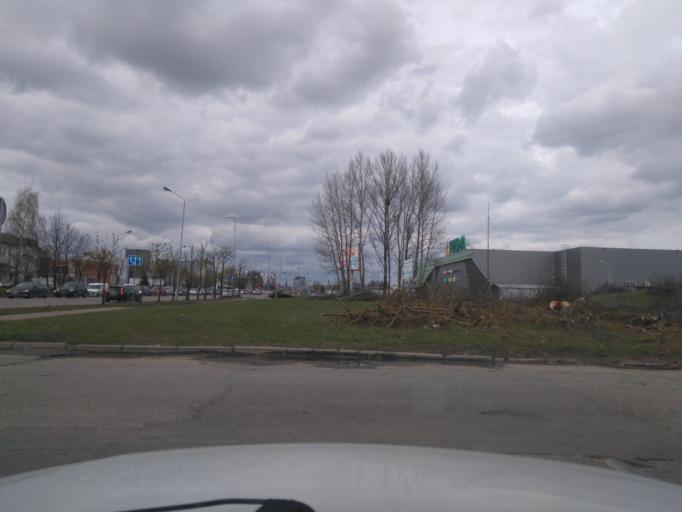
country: LT
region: Kauno apskritis
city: Dainava (Kaunas)
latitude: 54.9072
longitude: 23.9815
